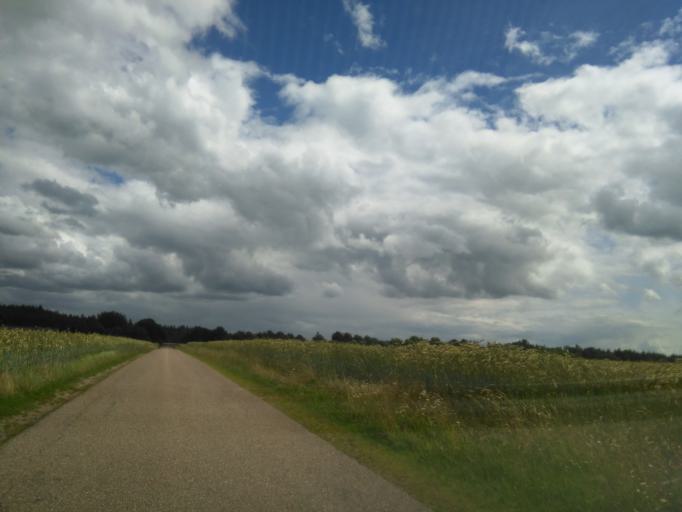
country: DK
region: Central Jutland
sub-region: Ikast-Brande Kommune
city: Bording Kirkeby
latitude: 56.0398
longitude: 9.3840
